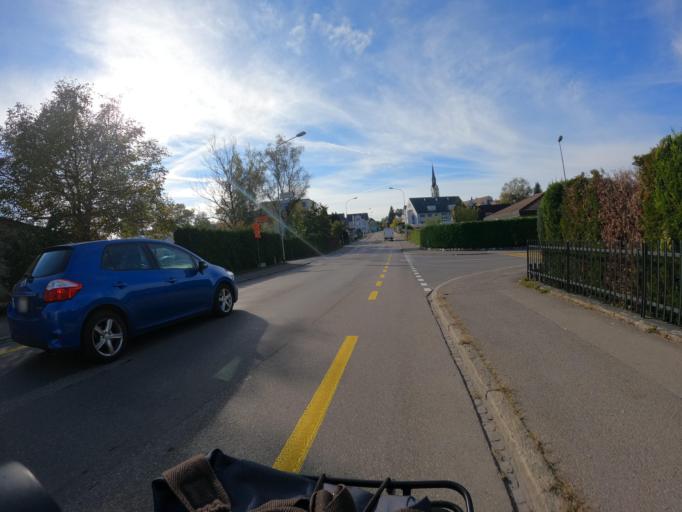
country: CH
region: Zurich
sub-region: Bezirk Affoltern
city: Obfelden
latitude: 47.2633
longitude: 8.4261
